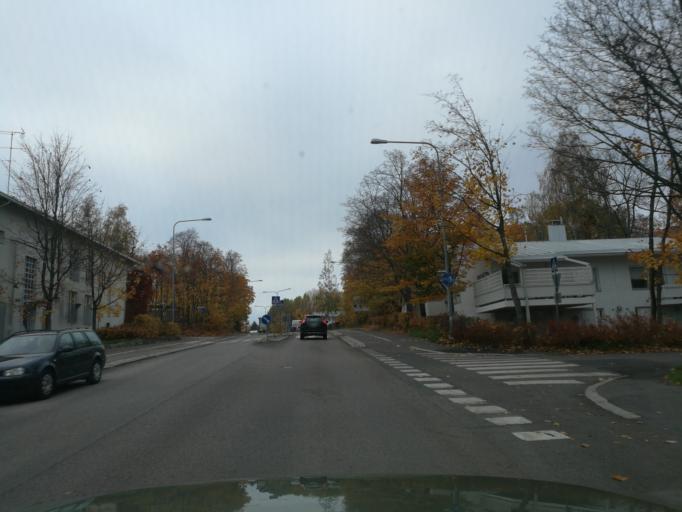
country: FI
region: Uusimaa
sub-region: Helsinki
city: Helsinki
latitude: 60.2329
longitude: 24.9673
